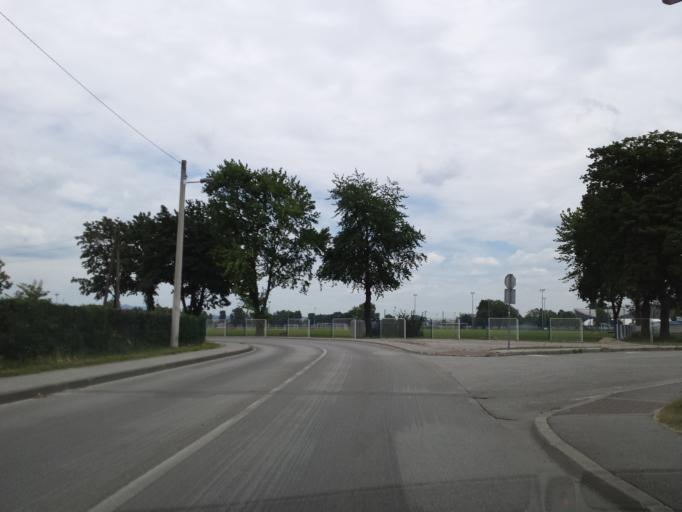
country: HR
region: Grad Zagreb
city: Novi Zagreb
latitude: 45.7809
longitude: 15.9664
